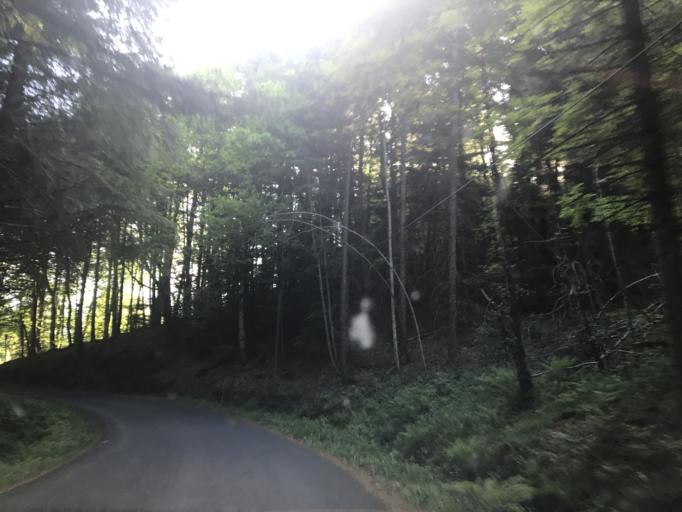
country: FR
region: Rhone-Alpes
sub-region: Departement de la Loire
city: Noiretable
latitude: 45.7393
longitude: 3.6894
